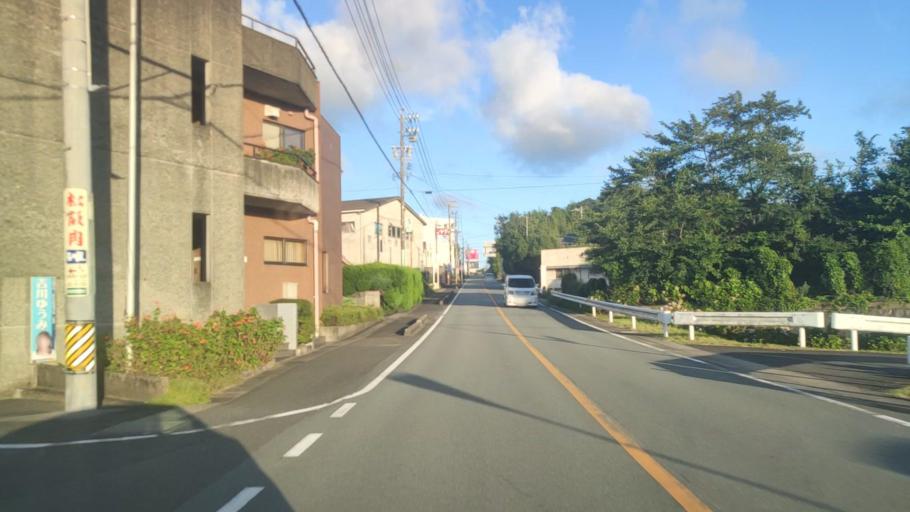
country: JP
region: Mie
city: Toba
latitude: 34.3273
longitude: 136.8239
